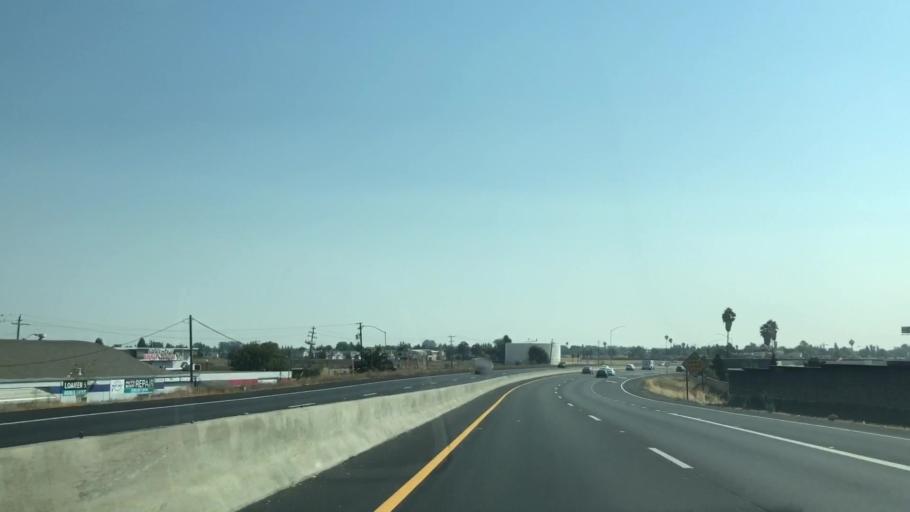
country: US
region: California
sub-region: Solano County
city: Fairfield
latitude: 38.2446
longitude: -122.0379
